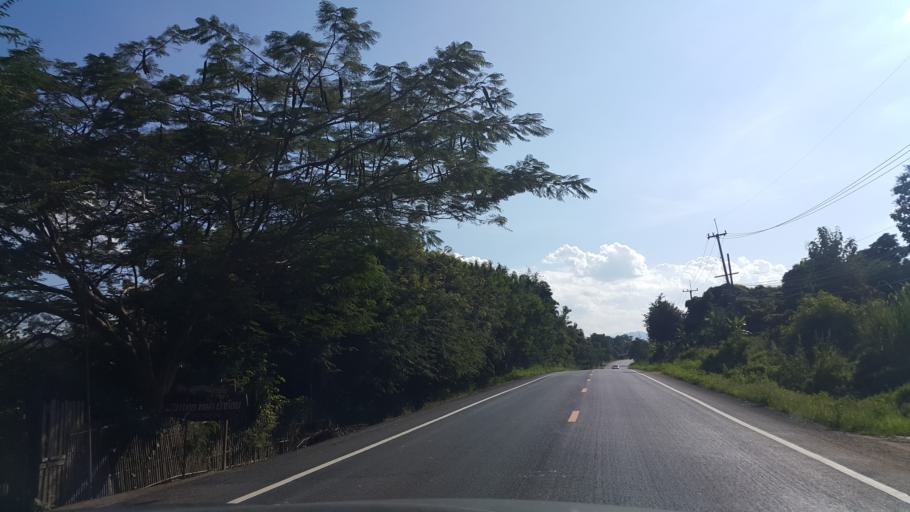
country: TH
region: Lamphun
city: Mae Tha
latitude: 18.4976
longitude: 99.1951
